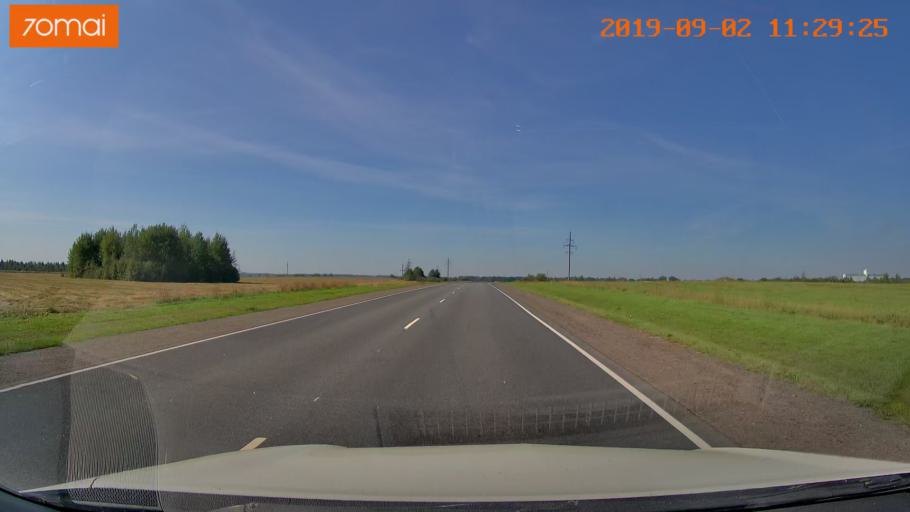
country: RU
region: Smolensk
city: Roslavl'
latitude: 53.9893
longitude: 32.8608
